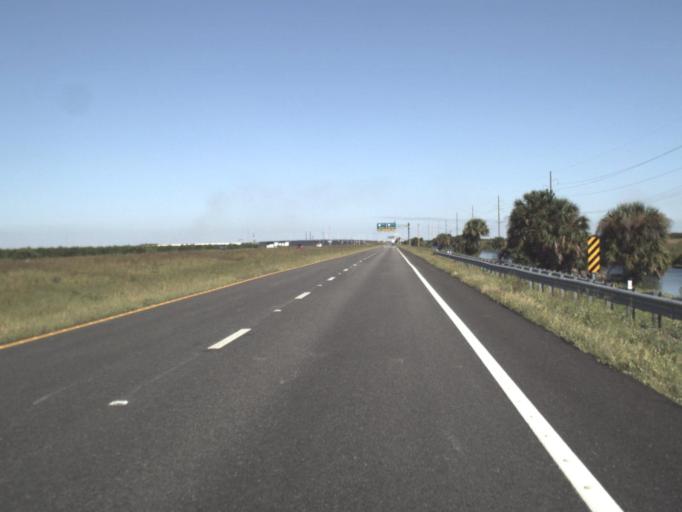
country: US
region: Florida
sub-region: Glades County
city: Moore Haven
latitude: 26.7532
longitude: -81.0970
